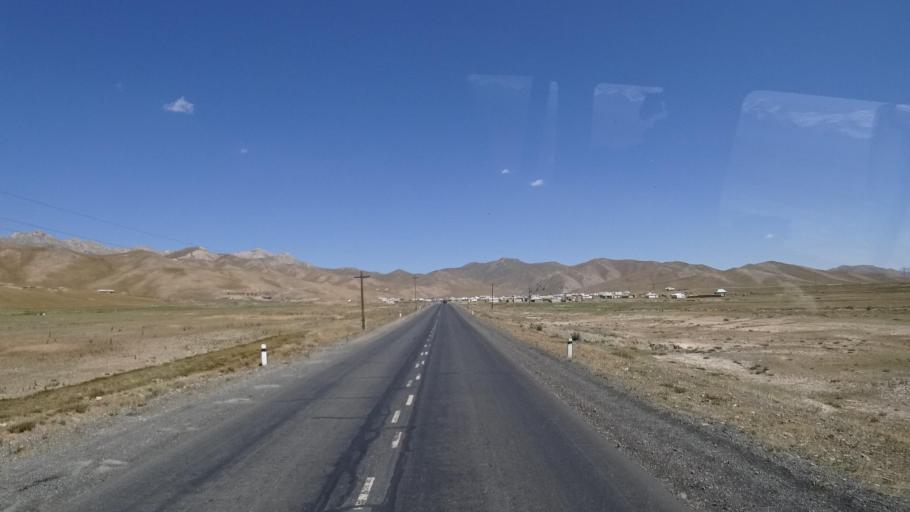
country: KG
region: Osh
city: Gul'cha
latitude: 39.7172
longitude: 73.2419
